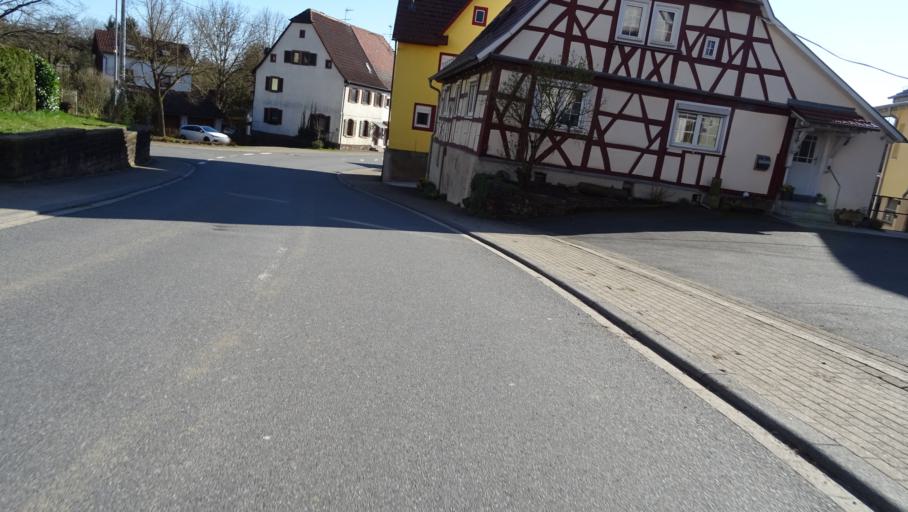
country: DE
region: Baden-Wuerttemberg
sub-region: Karlsruhe Region
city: Seckach
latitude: 49.4292
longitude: 9.2887
